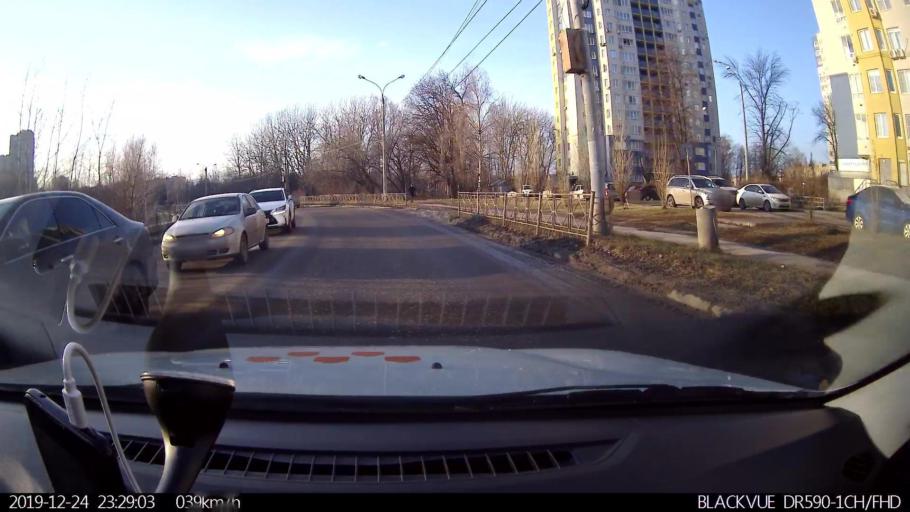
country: RU
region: Nizjnij Novgorod
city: Gorbatovka
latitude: 56.2396
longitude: 43.8466
